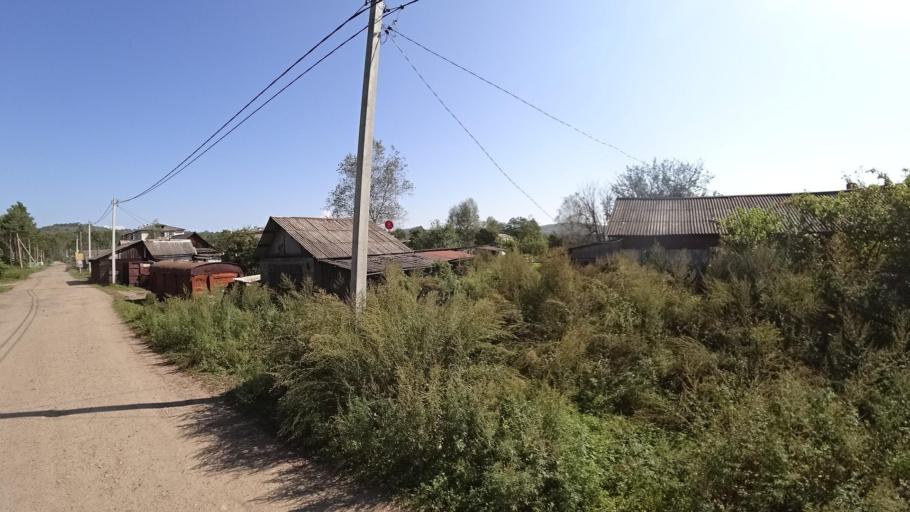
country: RU
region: Jewish Autonomous Oblast
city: Bira
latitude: 48.9960
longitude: 132.4544
